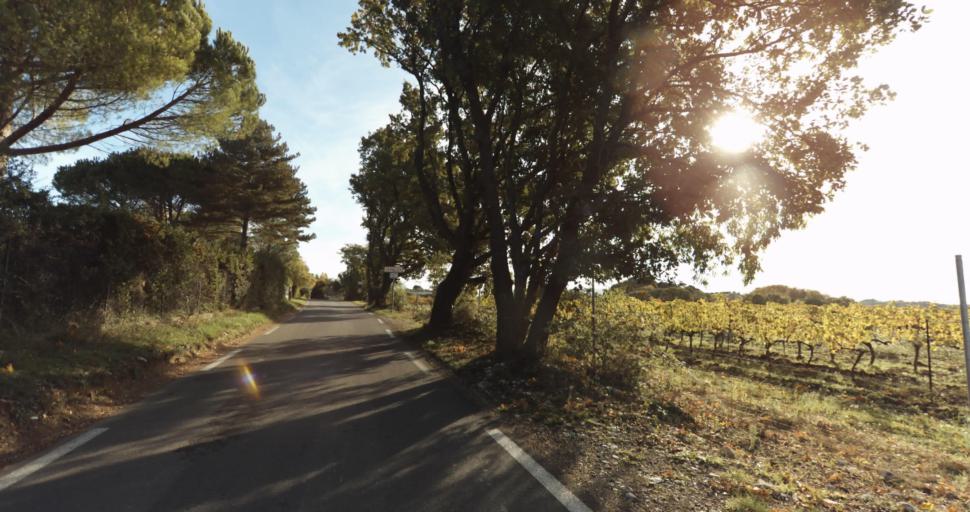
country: FR
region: Provence-Alpes-Cote d'Azur
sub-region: Departement des Bouches-du-Rhone
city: Venelles
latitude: 43.5894
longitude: 5.4649
